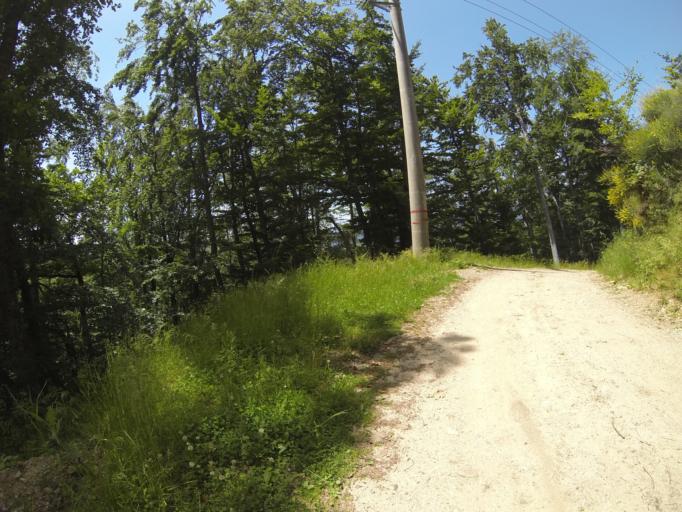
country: RO
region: Valcea
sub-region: Oras Baile Olanesti
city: Baile Olanesti
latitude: 45.2118
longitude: 24.2051
